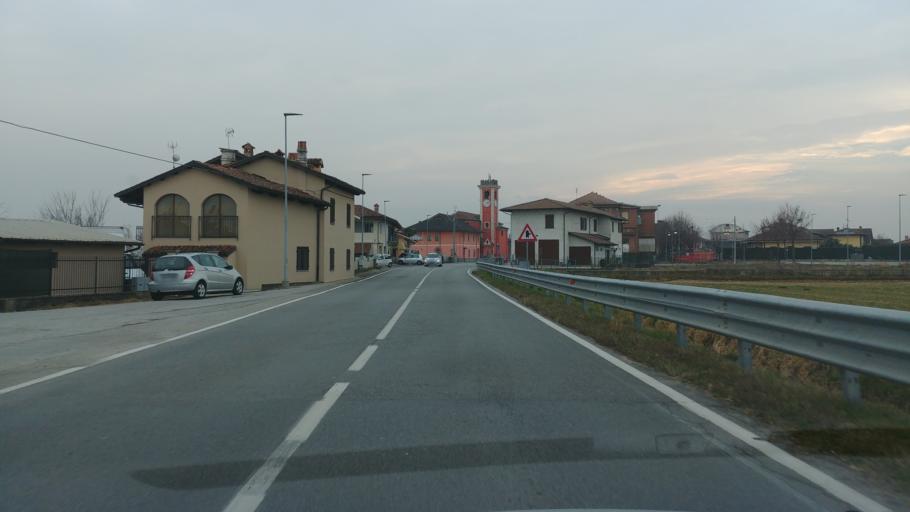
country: IT
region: Piedmont
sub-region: Provincia di Cuneo
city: Sant'Albano Stura
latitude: 44.5126
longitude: 7.6904
